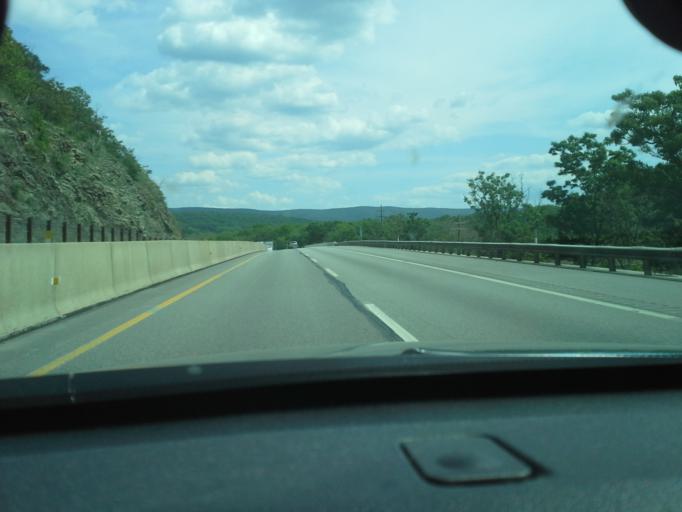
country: US
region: Pennsylvania
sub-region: Bedford County
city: Bedford
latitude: 40.0158
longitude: -78.4716
